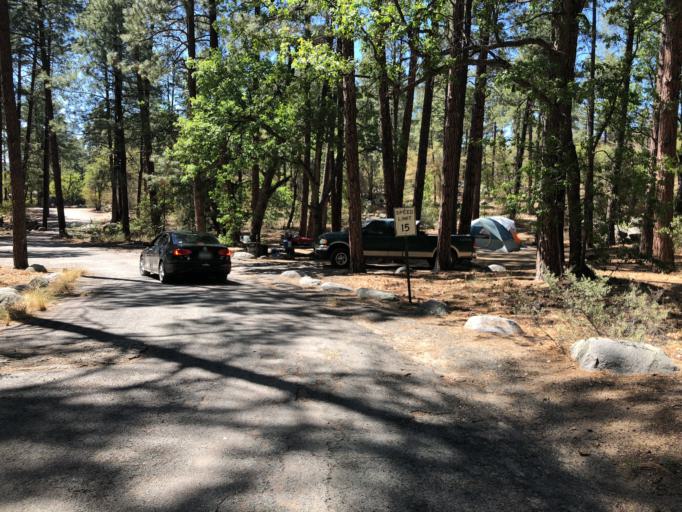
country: US
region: Arizona
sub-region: Yavapai County
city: Prescott
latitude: 34.4547
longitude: -112.4593
